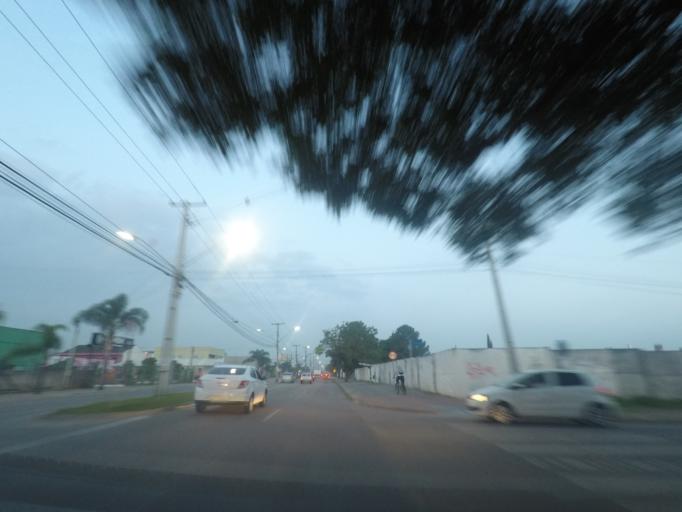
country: BR
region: Parana
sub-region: Pinhais
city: Pinhais
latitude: -25.4526
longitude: -49.1754
